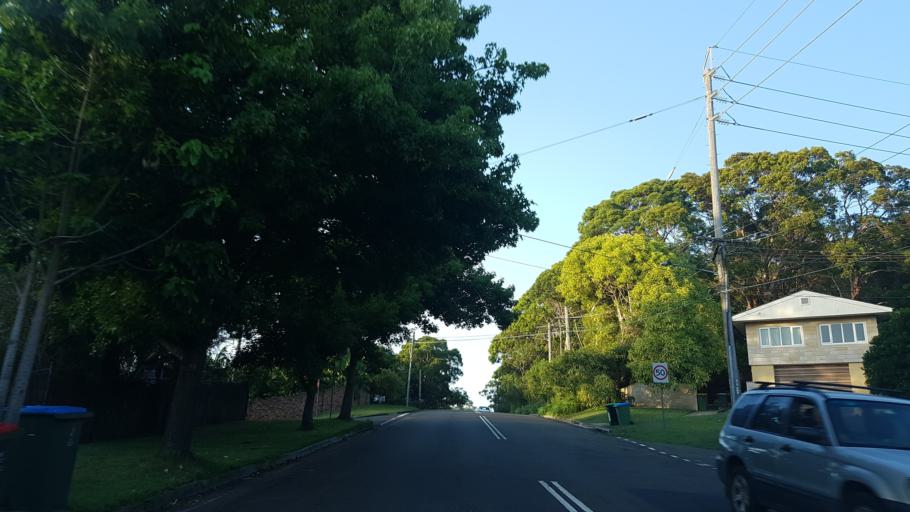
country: AU
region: New South Wales
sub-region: Warringah
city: Narraweena
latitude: -33.7381
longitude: 151.2703
